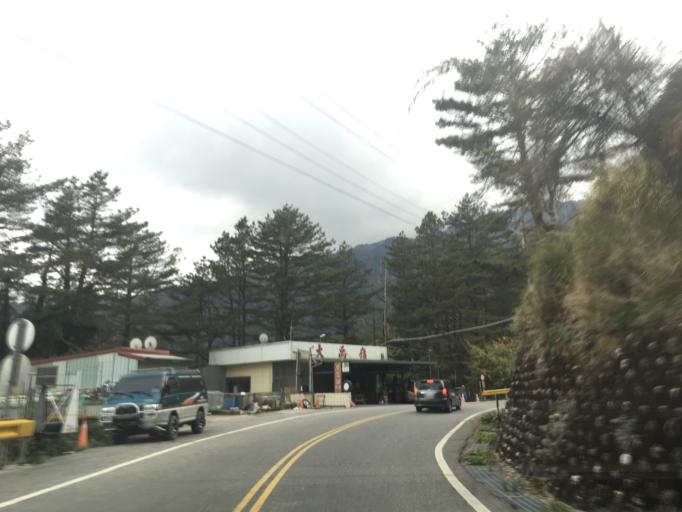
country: TW
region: Taiwan
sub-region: Hualien
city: Hualian
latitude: 24.1800
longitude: 121.3104
